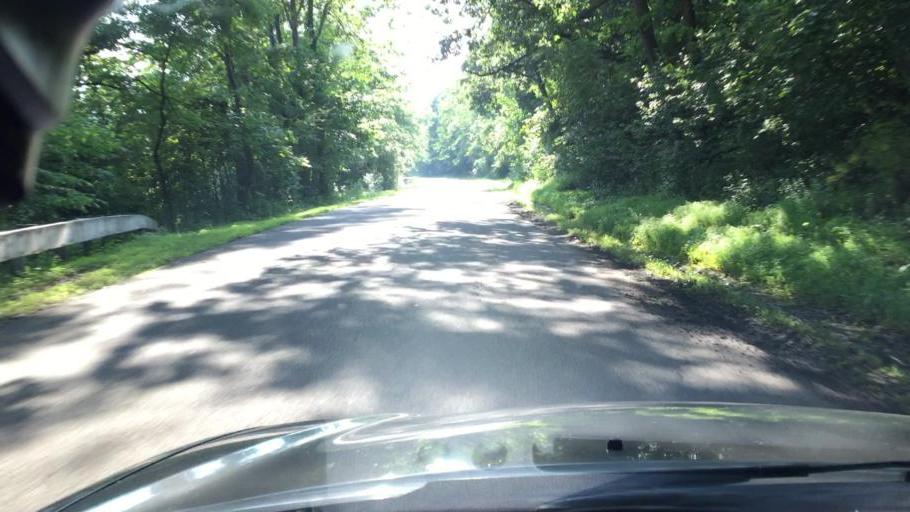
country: US
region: Pennsylvania
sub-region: Carbon County
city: Jim Thorpe
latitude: 40.8751
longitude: -75.7461
